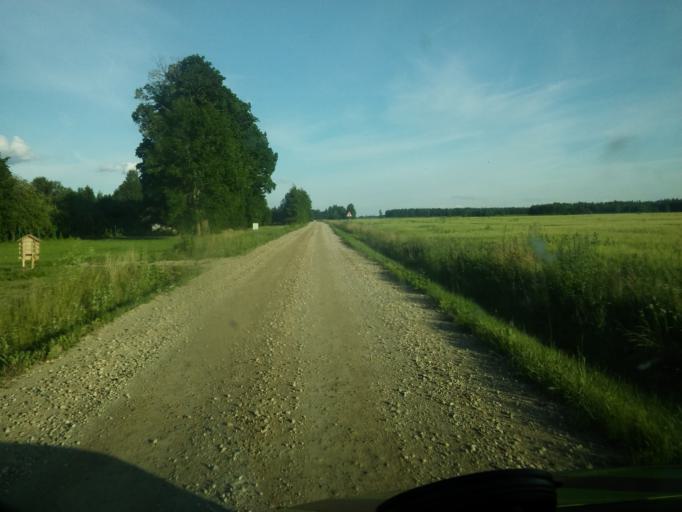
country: EE
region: Valgamaa
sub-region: Torva linn
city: Torva
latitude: 58.0672
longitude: 25.9058
